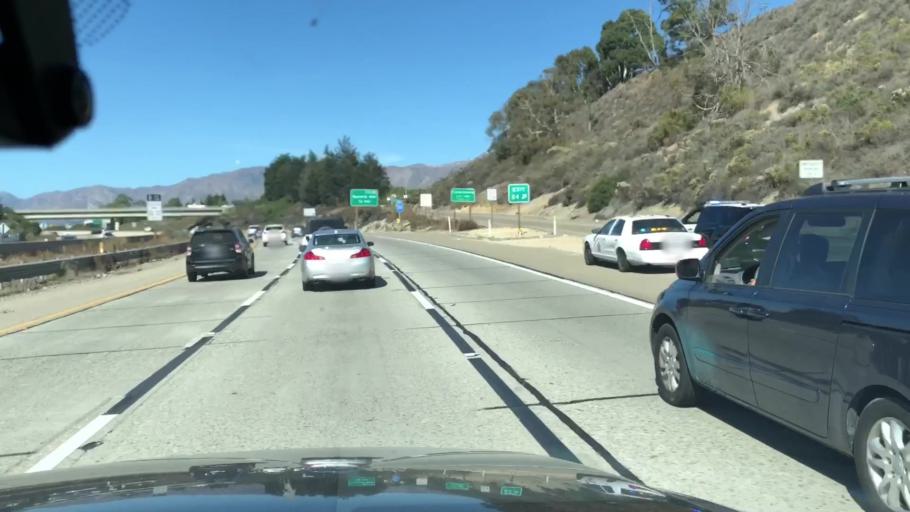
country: US
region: California
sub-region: Santa Barbara County
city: Carpinteria
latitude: 34.3818
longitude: -119.4825
